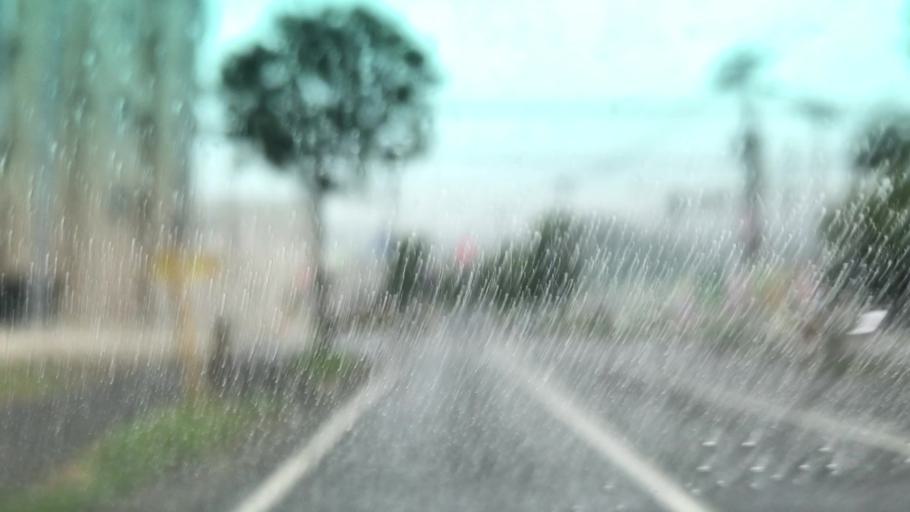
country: JP
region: Hokkaido
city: Sapporo
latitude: 43.0638
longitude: 141.3036
